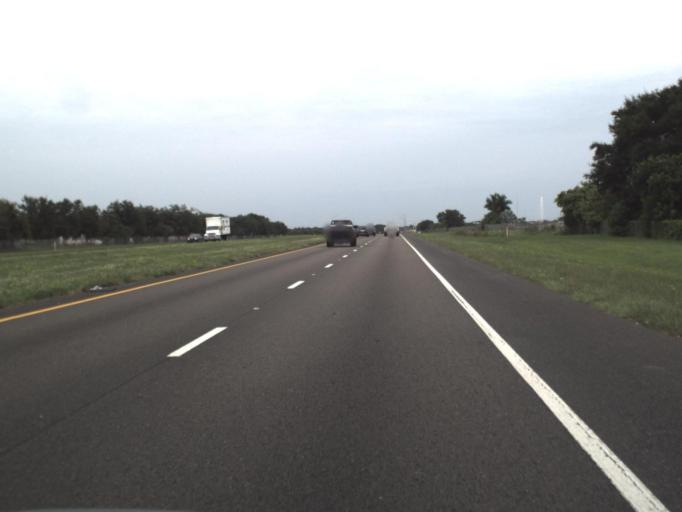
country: US
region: Florida
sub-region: Manatee County
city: Whitfield
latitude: 27.4099
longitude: -82.5327
